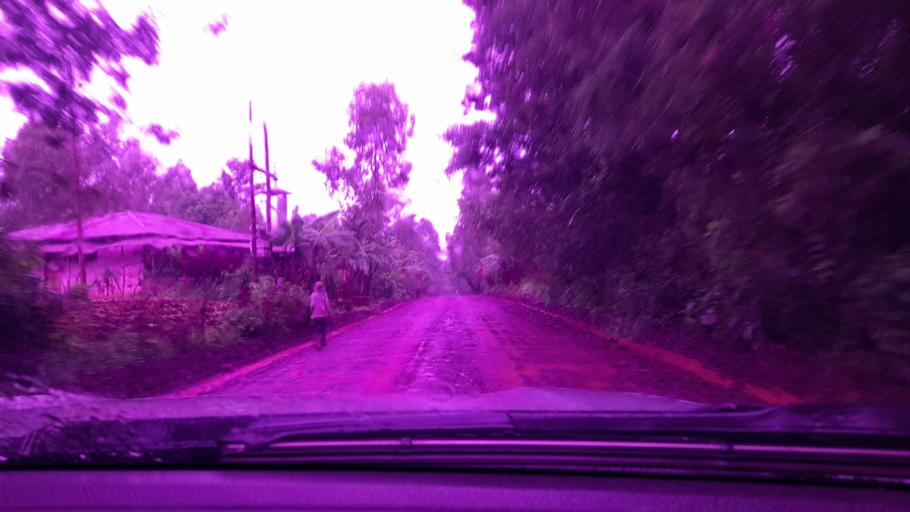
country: ET
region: Oromiya
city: Metu
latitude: 8.3389
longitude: 35.6035
